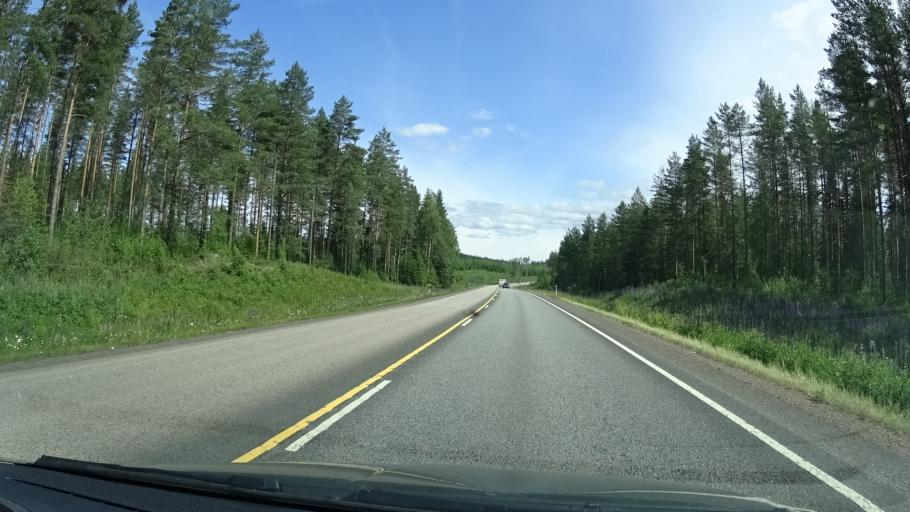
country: FI
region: Central Finland
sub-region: Jyvaeskylae
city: Muurame
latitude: 62.2650
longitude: 25.4811
